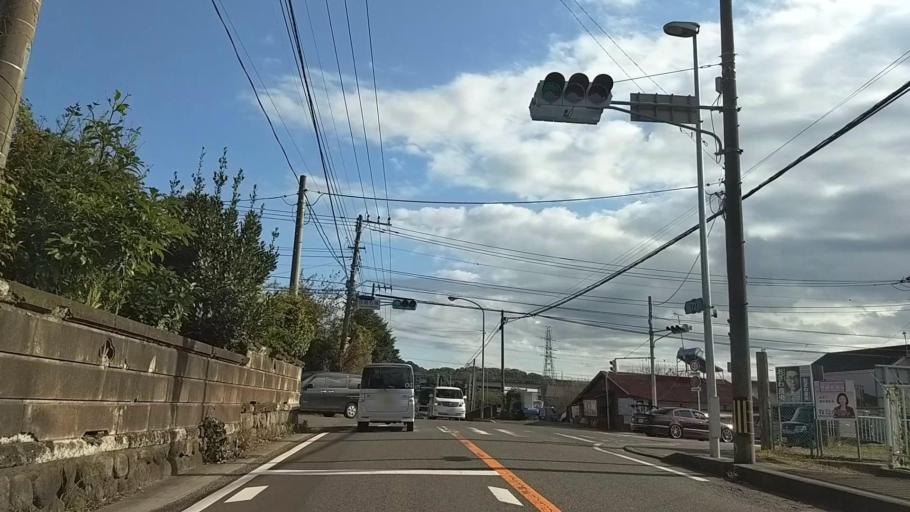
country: JP
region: Kanagawa
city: Ninomiya
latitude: 35.2924
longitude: 139.2011
